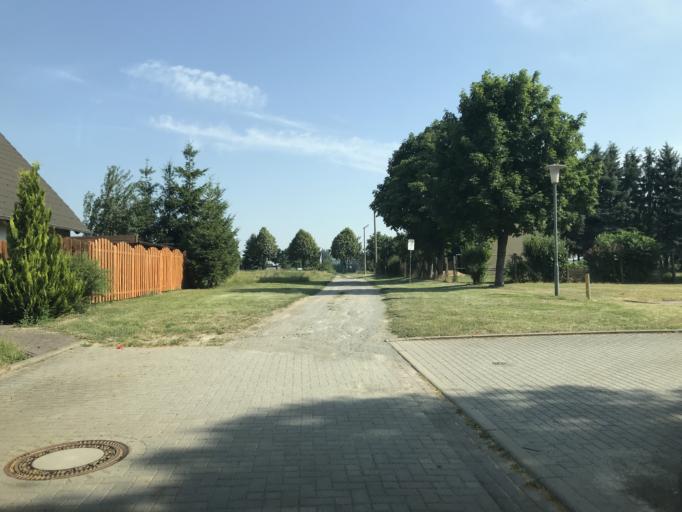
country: DE
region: Saxony-Anhalt
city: Altenhausen
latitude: 52.2568
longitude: 11.2223
